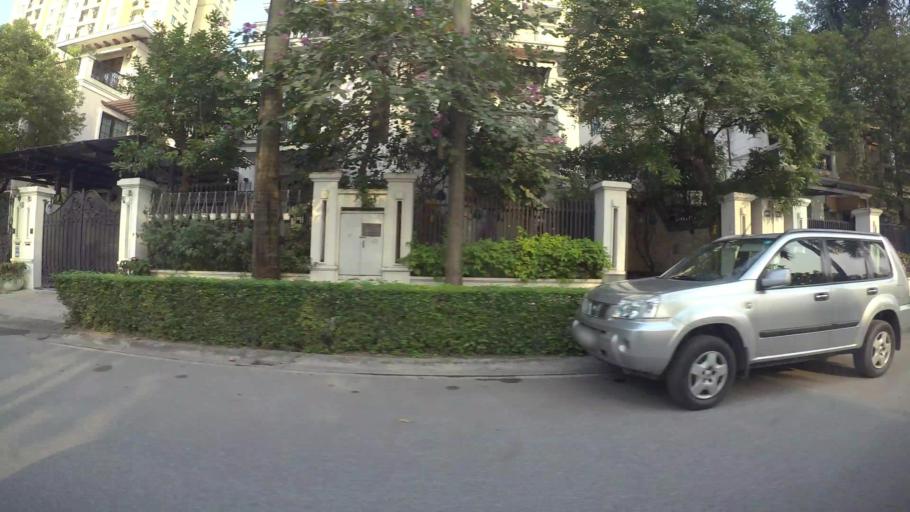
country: VN
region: Ha Noi
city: Tay Ho
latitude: 21.0742
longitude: 105.8093
